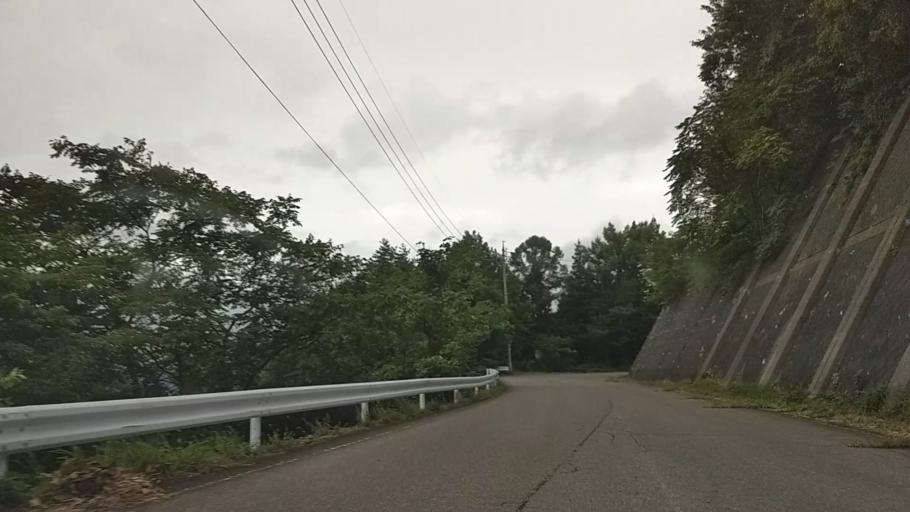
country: JP
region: Nagano
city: Iiyama
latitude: 36.8157
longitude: 138.3719
